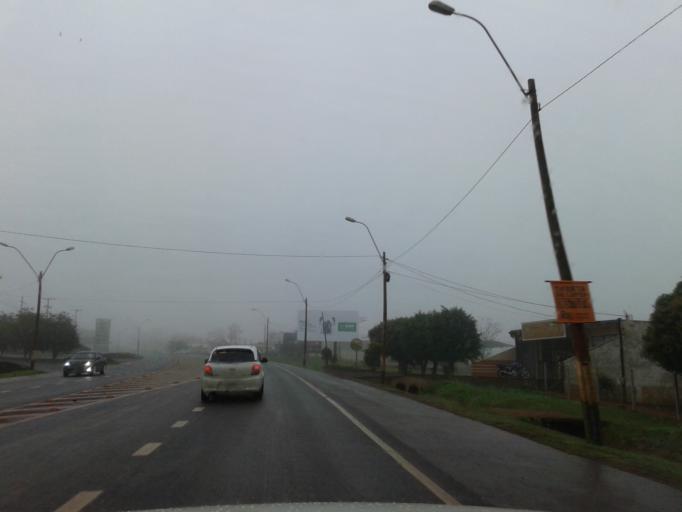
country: PY
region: Itapua
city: Arquitecto Tomas Romero Pereira
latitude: -26.5471
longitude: -55.2571
